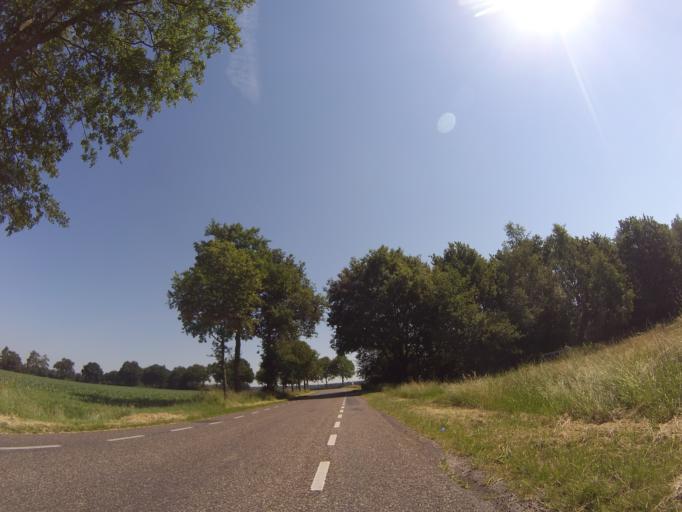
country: NL
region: Drenthe
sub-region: Gemeente Coevorden
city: Sleen
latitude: 52.8085
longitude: 6.7378
